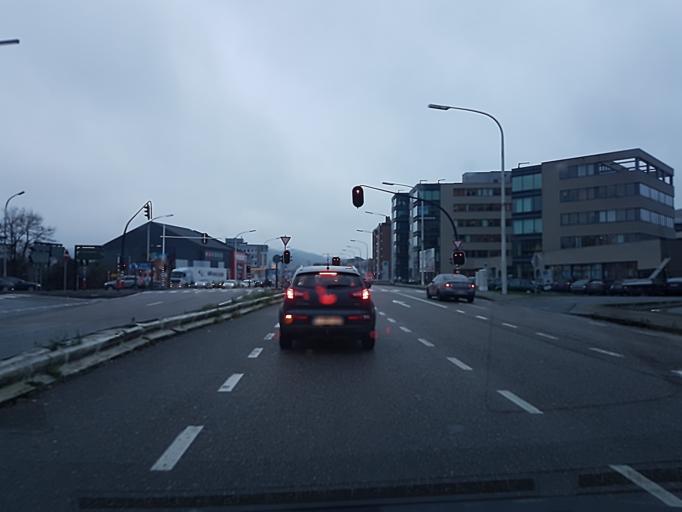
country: BE
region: Wallonia
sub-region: Province de Namur
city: Namur
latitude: 50.4639
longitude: 4.8877
